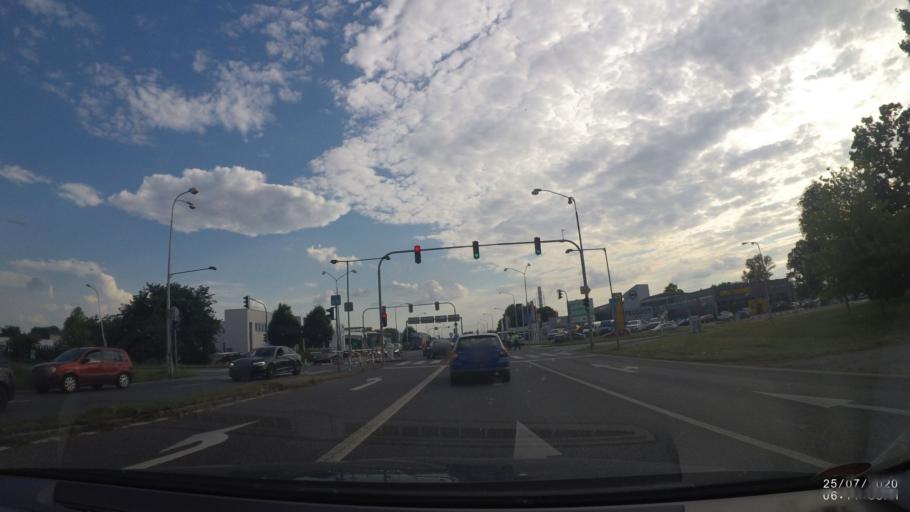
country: CZ
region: Kralovehradecky
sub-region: Okres Hradec Kralove
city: Hradec Kralove
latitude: 50.1967
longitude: 15.8144
